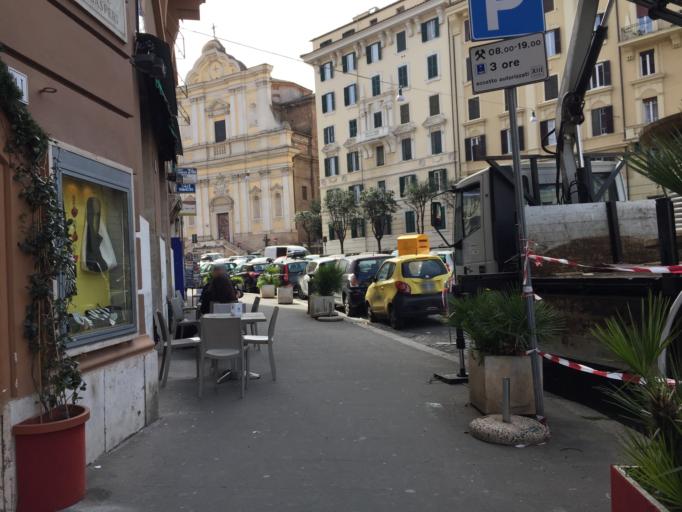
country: VA
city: Vatican City
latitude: 41.8986
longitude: 12.4555
